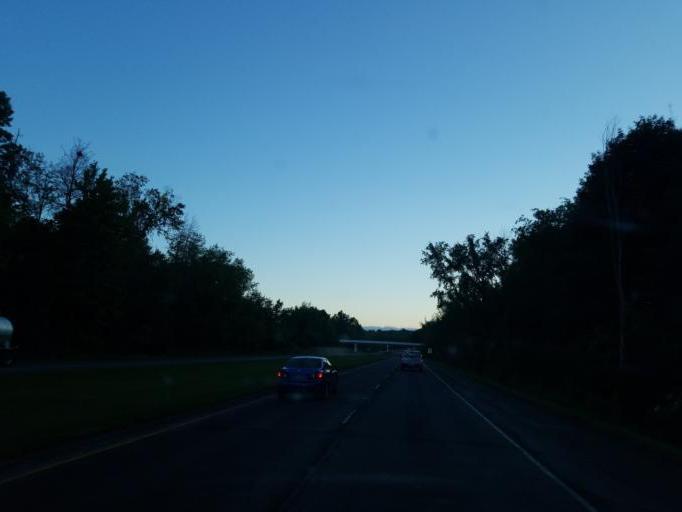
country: US
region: Ohio
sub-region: Summit County
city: Norton
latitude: 41.0230
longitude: -81.6653
